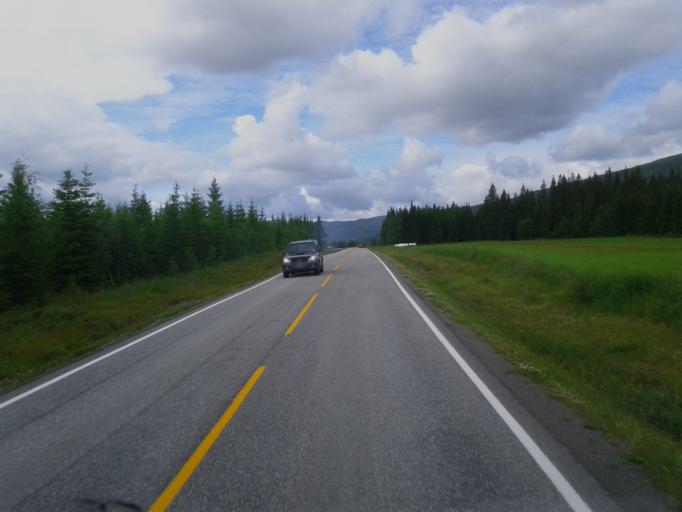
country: NO
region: Nord-Trondelag
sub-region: Hoylandet
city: Hoylandet
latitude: 64.6623
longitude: 12.6568
